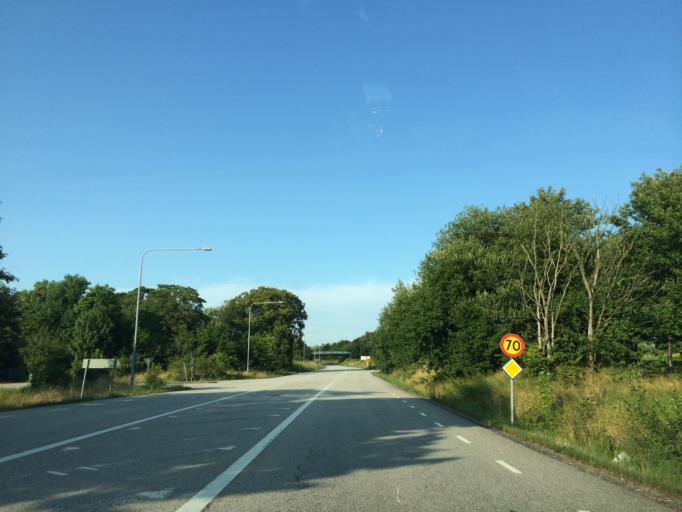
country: SE
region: Skane
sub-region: Malmo
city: Oxie
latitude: 55.5842
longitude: 13.0990
